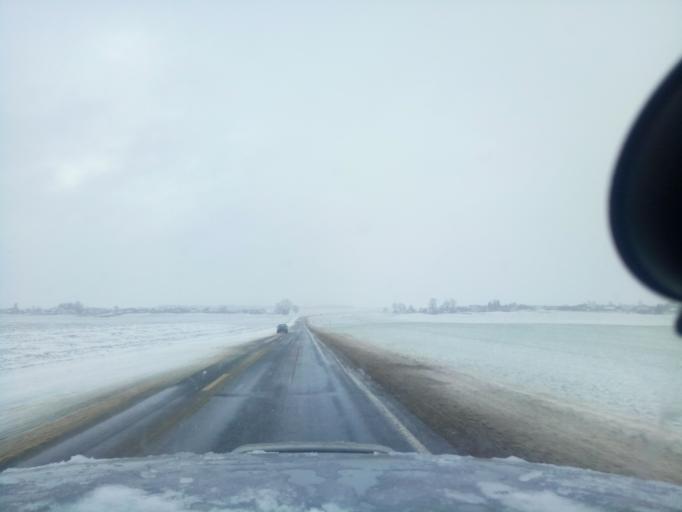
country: BY
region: Minsk
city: Haradzyeya
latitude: 53.3096
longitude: 26.5681
